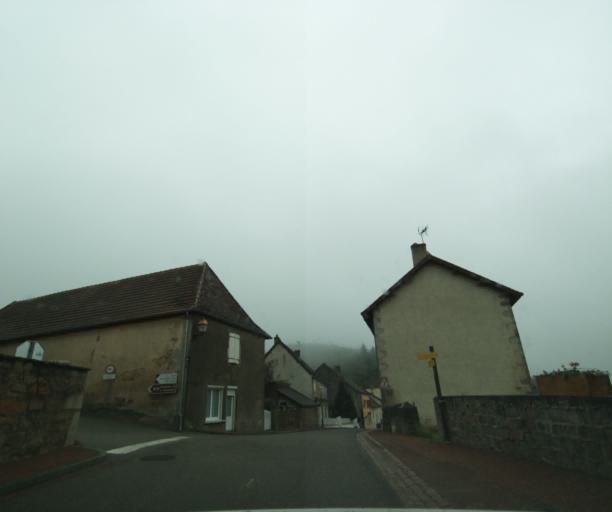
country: FR
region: Bourgogne
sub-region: Departement de Saone-et-Loire
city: Charolles
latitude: 46.4021
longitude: 4.3986
